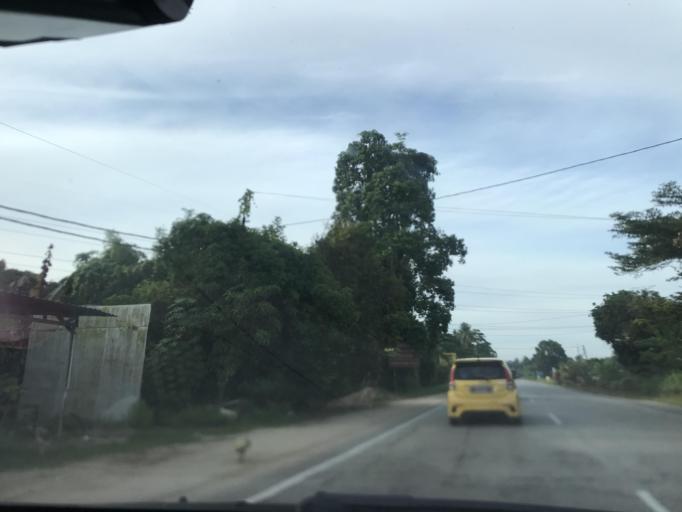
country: MY
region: Kelantan
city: Kampong Kadok
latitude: 5.9911
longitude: 102.1891
